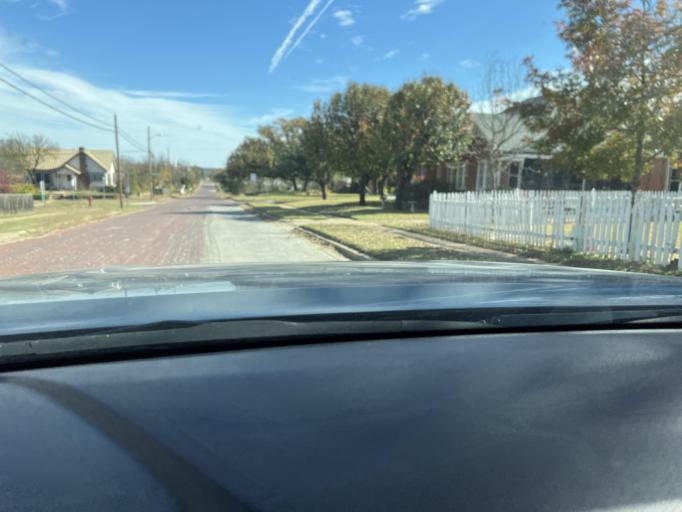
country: US
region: Texas
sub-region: Eastland County
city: Eastland
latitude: 32.3995
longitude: -98.8262
